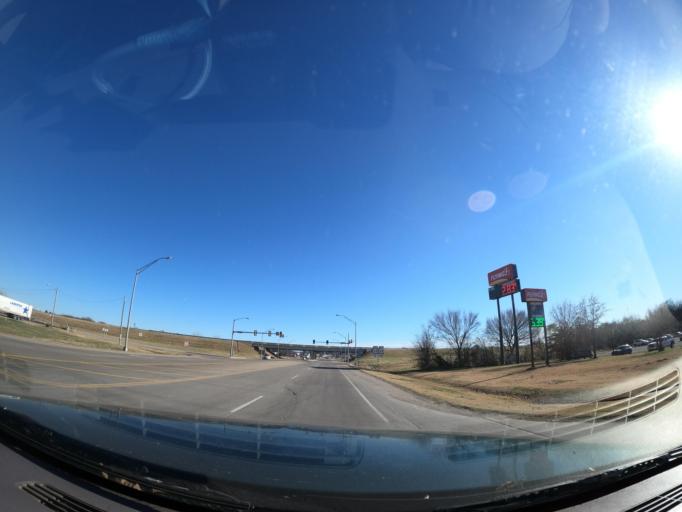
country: US
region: Oklahoma
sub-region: McIntosh County
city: Checotah
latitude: 35.4761
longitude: -95.5379
